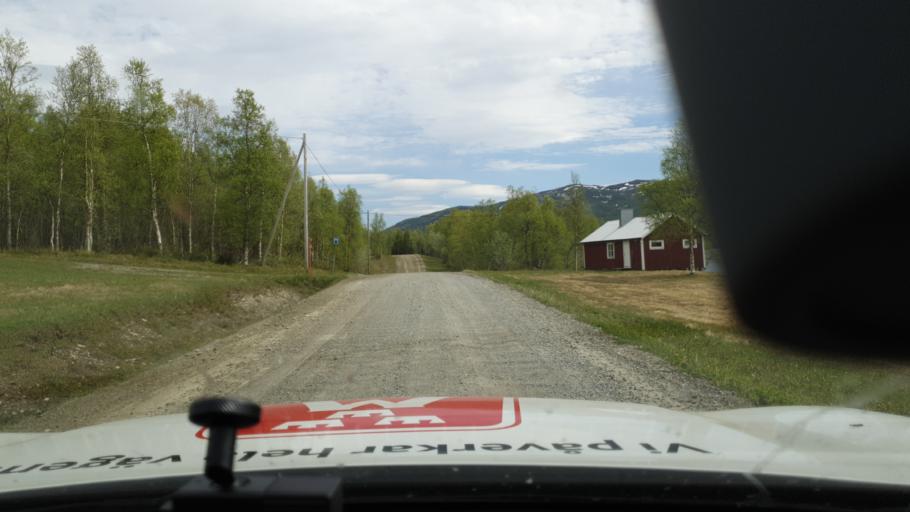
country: NO
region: Nordland
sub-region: Rana
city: Mo i Rana
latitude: 65.7513
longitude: 15.2061
